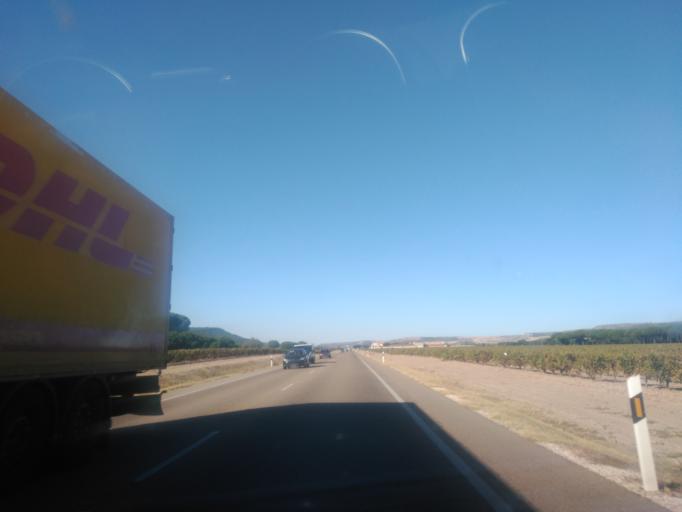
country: ES
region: Castille and Leon
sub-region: Provincia de Valladolid
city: Valbuena de Duero
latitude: 41.6283
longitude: -4.3058
